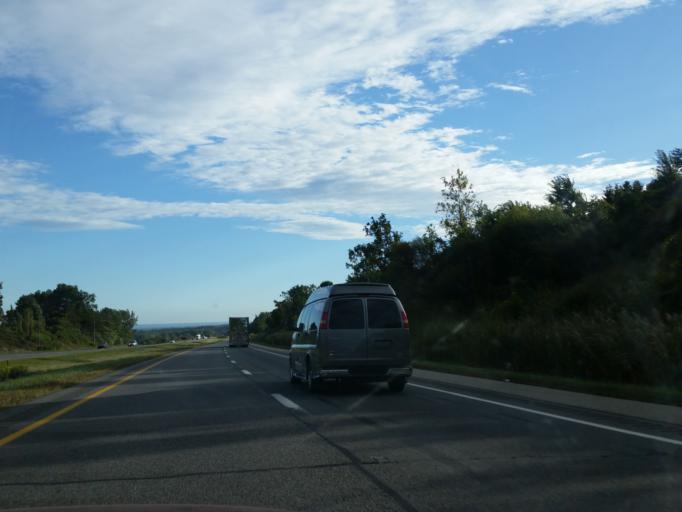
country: US
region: Pennsylvania
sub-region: Erie County
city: North East
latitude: 42.1817
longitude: -79.8377
